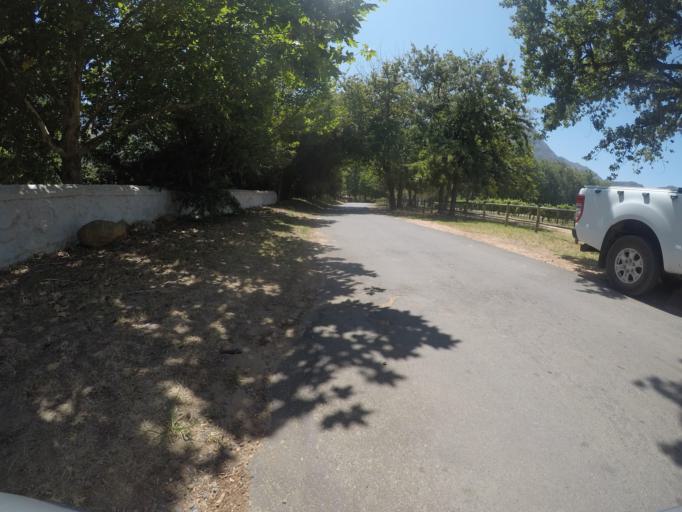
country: ZA
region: Western Cape
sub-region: Cape Winelands District Municipality
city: Stellenbosch
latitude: -33.9965
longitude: 18.8750
